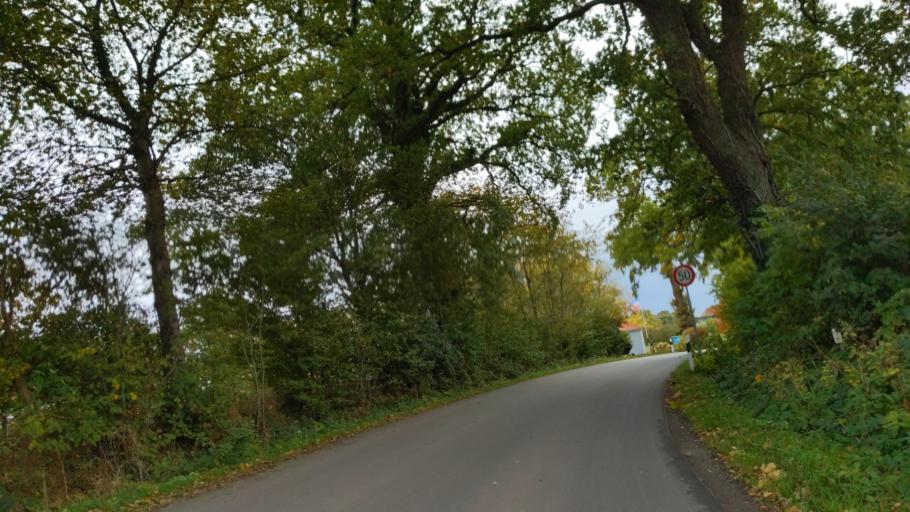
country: DE
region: Schleswig-Holstein
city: Sierksdorf
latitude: 54.0826
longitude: 10.7449
